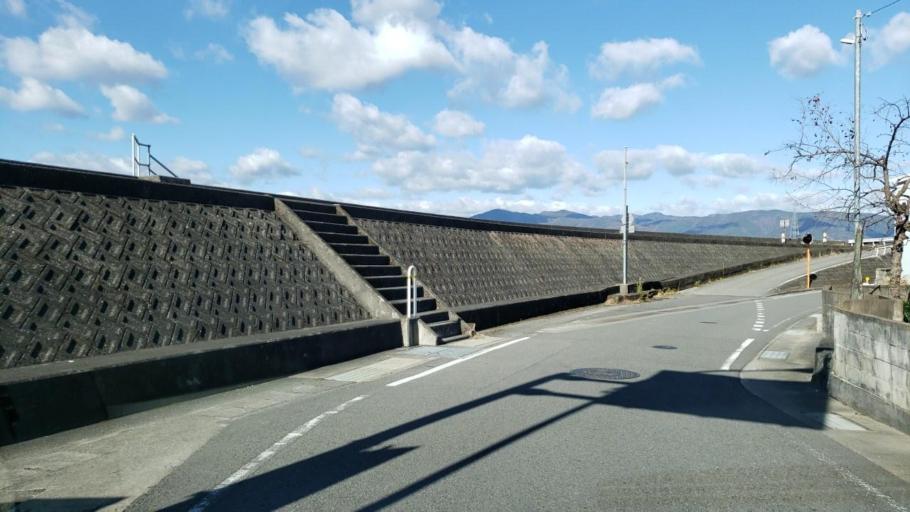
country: JP
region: Tokushima
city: Kamojimacho-jogejima
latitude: 34.0660
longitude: 134.3172
